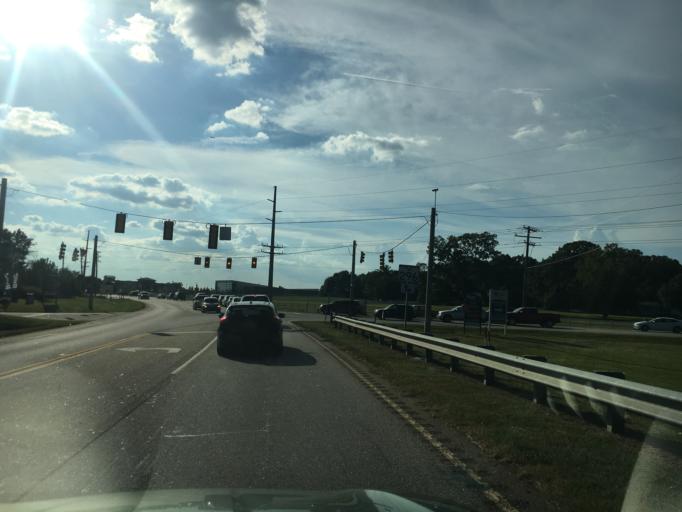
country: US
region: South Carolina
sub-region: Greenville County
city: Five Forks
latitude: 34.8072
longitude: -82.2177
